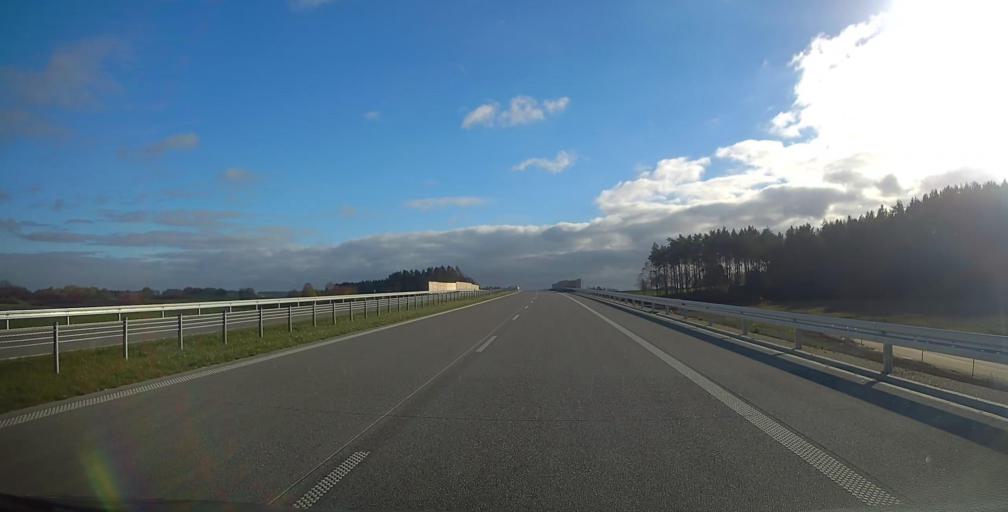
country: PL
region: Podlasie
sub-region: Powiat grajewski
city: Szczuczyn
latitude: 53.7060
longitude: 22.2841
